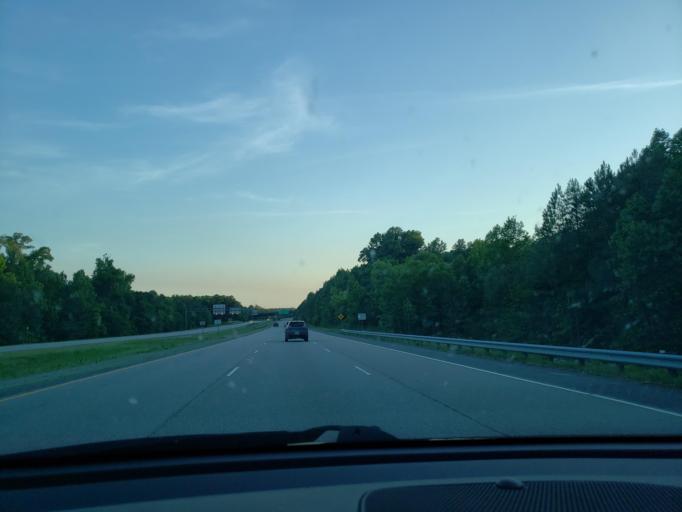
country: US
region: Virginia
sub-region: Chesterfield County
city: Bensley
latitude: 37.4549
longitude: -77.3899
